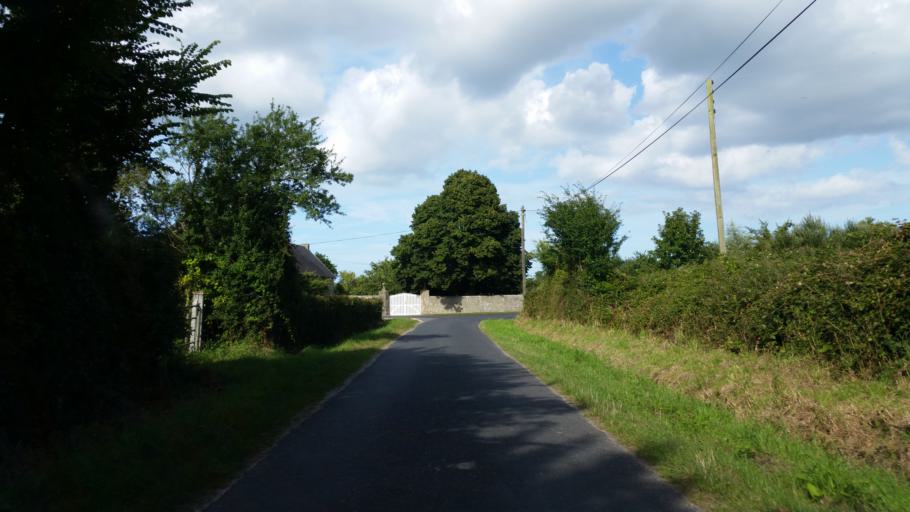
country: FR
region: Lower Normandy
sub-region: Departement de la Manche
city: Sainte-Mere-Eglise
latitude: 49.4498
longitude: -1.2546
